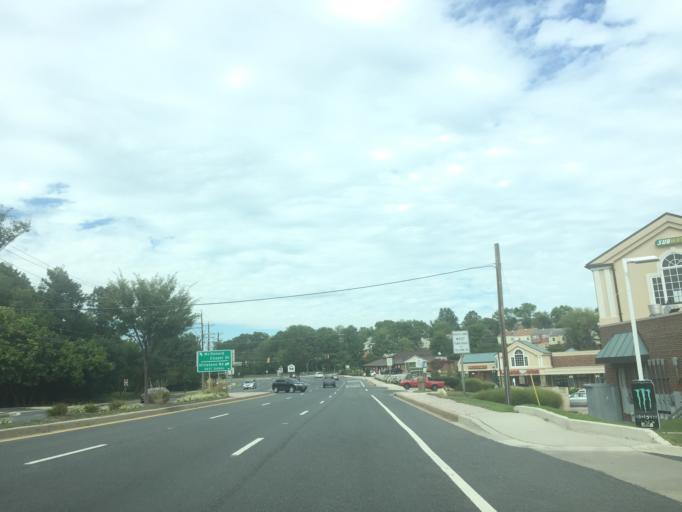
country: US
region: Maryland
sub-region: Montgomery County
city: North Potomac
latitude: 39.1182
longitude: -77.2522
